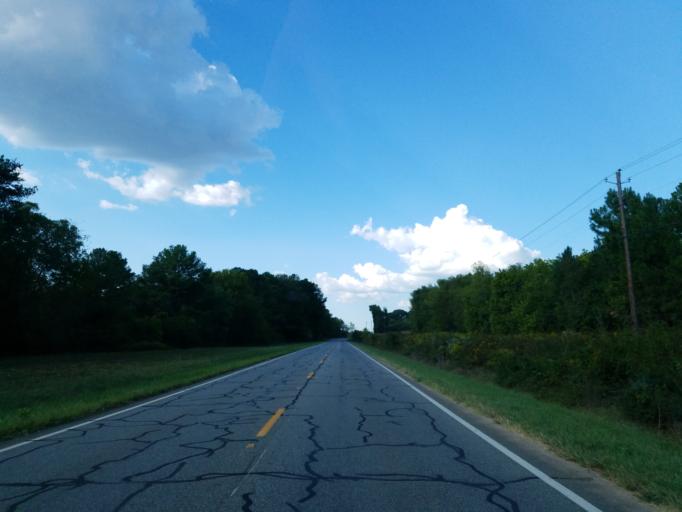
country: US
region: Georgia
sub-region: Bartow County
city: Rydal
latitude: 34.5119
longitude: -84.7101
